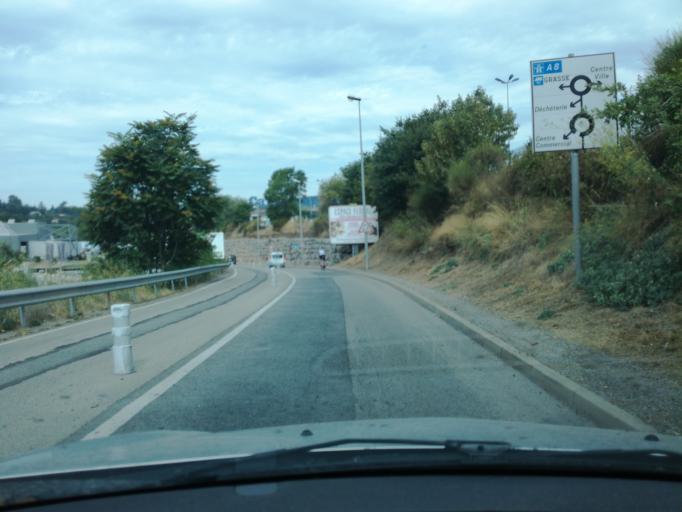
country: FR
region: Provence-Alpes-Cote d'Azur
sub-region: Departement du Var
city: Draguignan
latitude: 43.5271
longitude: 6.4533
